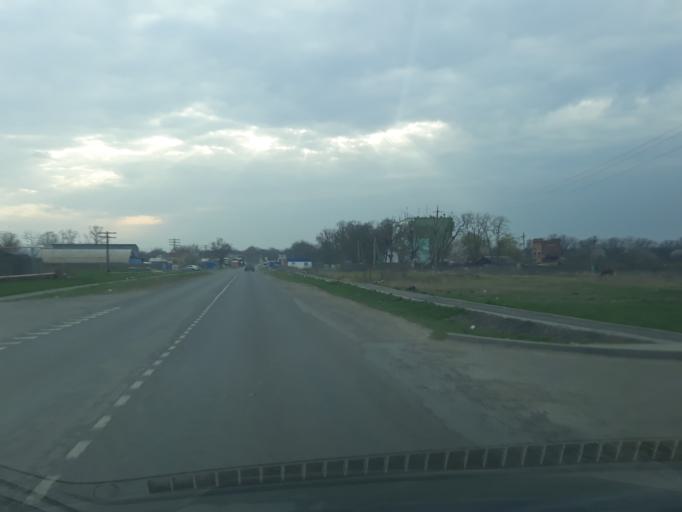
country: RU
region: Rostov
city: Novobessergenovka
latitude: 47.1799
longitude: 38.8044
